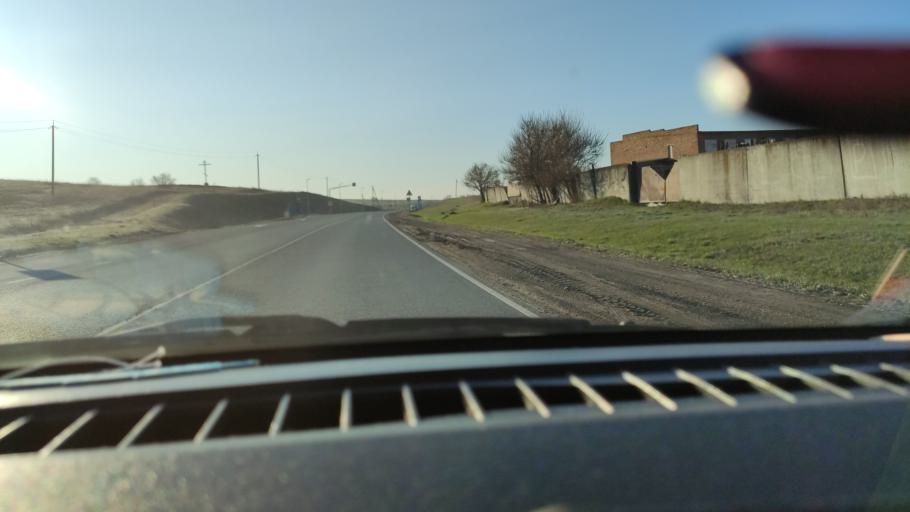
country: RU
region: Saratov
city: Tersa
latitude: 52.0959
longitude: 47.5378
